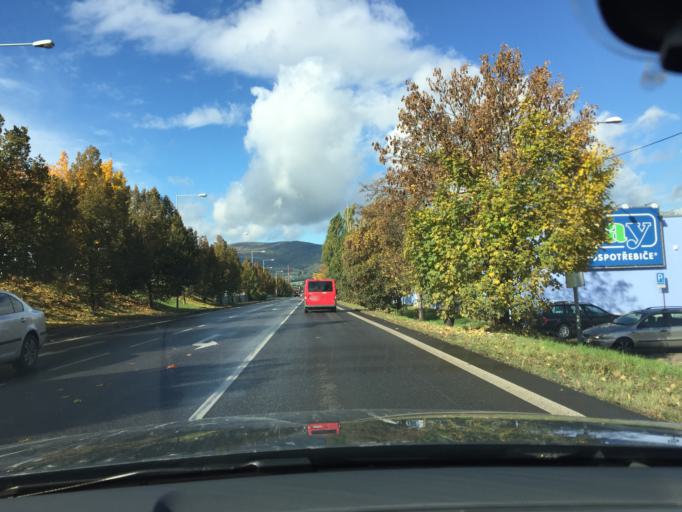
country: CZ
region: Ustecky
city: Trmice
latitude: 50.6886
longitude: 13.9867
